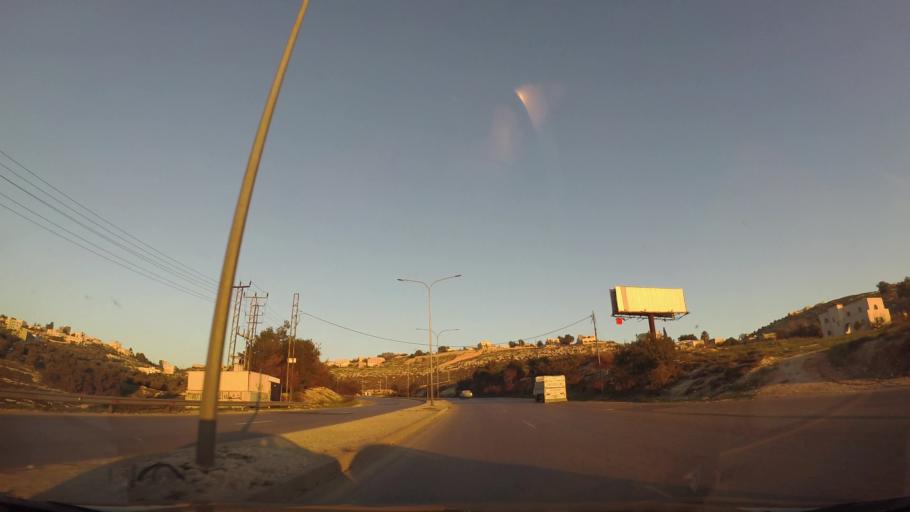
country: JO
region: Amman
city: Umm as Summaq
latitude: 31.8605
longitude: 35.8090
